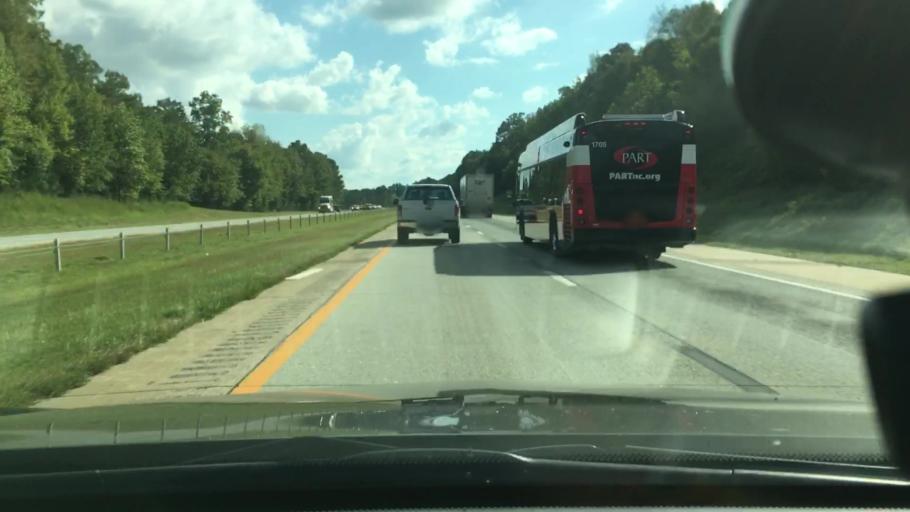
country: US
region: North Carolina
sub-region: Orange County
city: Chapel Hill
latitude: 35.9929
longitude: -79.0755
